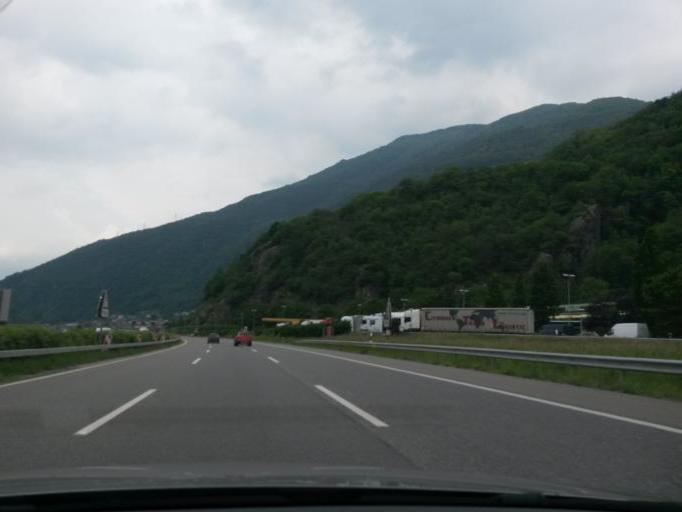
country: CH
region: Ticino
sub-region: Bellinzona District
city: Bellinzona
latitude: 46.2096
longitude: 9.0299
